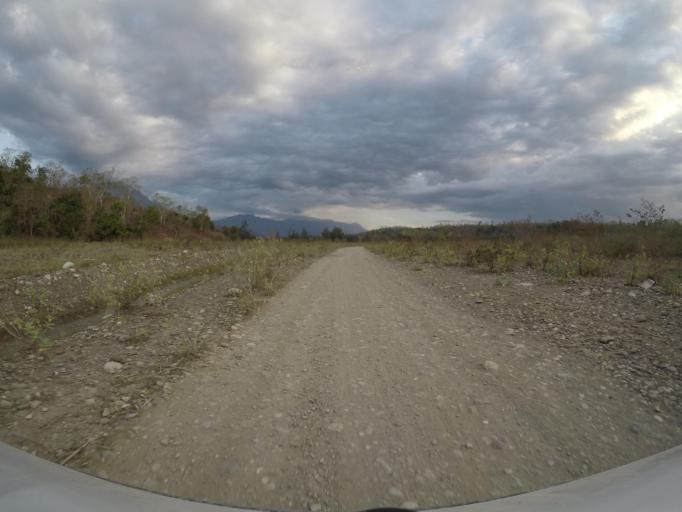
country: TL
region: Bobonaro
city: Maliana
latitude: -8.8980
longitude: 125.2091
